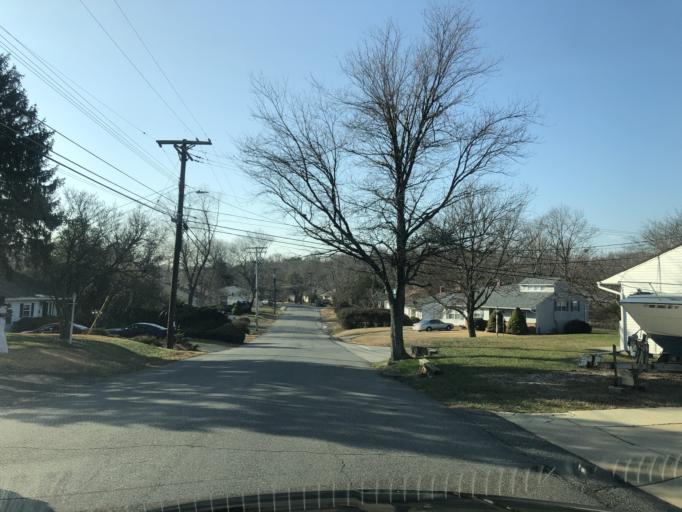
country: US
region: Maryland
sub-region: Anne Arundel County
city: Odenton
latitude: 39.0768
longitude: -76.7012
